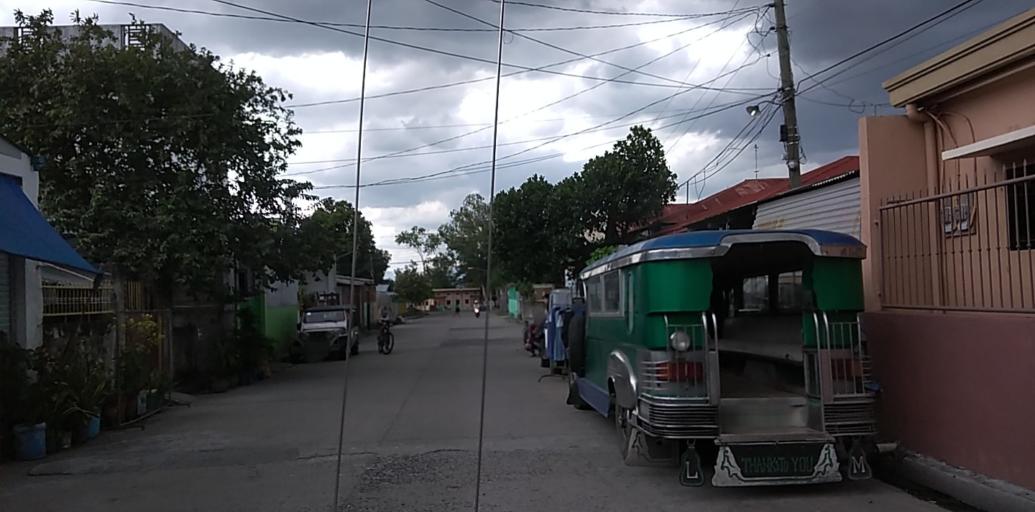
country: PH
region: Central Luzon
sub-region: Province of Pampanga
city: Pio
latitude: 15.0449
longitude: 120.5310
